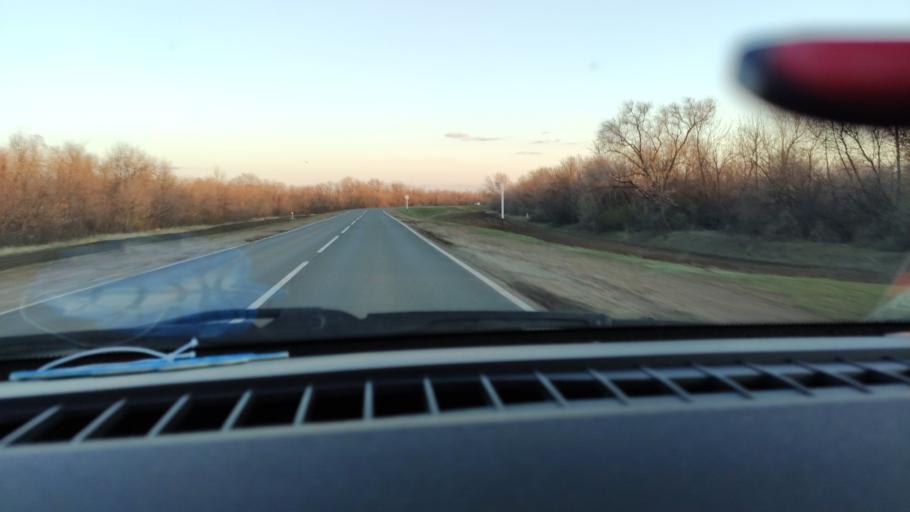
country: RU
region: Saratov
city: Privolzhskiy
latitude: 51.3682
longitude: 46.0465
